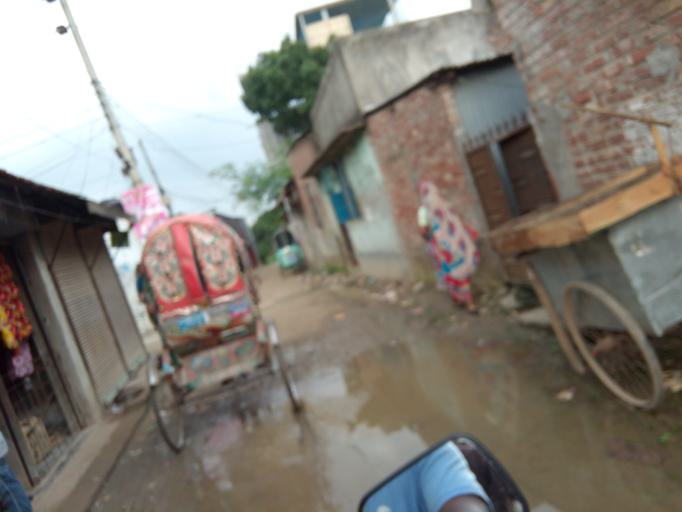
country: BD
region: Dhaka
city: Paltan
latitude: 23.7465
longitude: 90.4523
